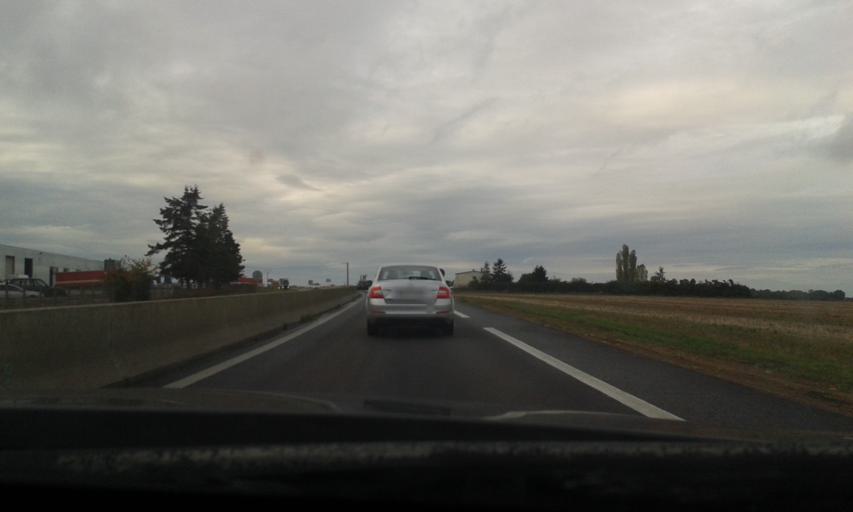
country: FR
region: Haute-Normandie
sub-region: Departement de l'Eure
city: La Madeleine-de-Nonancourt
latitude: 48.7781
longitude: 1.2082
